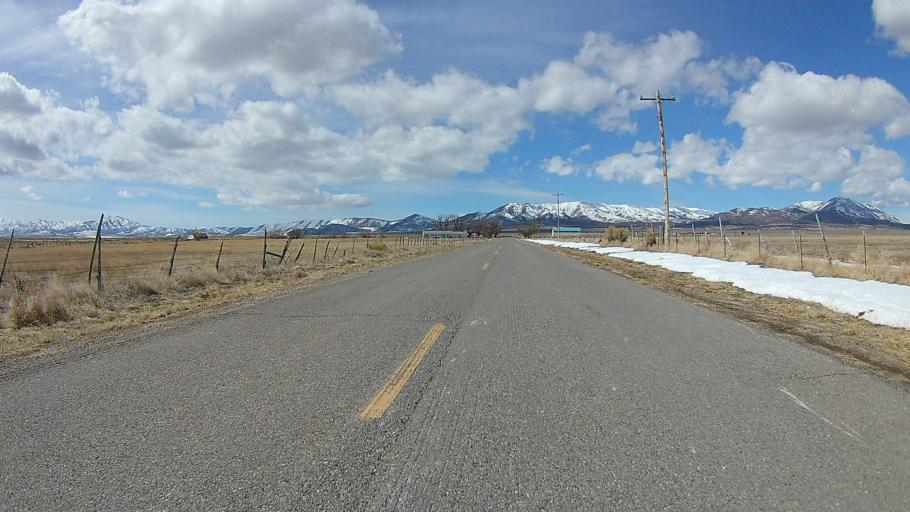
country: US
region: Utah
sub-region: Tooele County
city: Tooele
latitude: 40.1736
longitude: -112.4217
